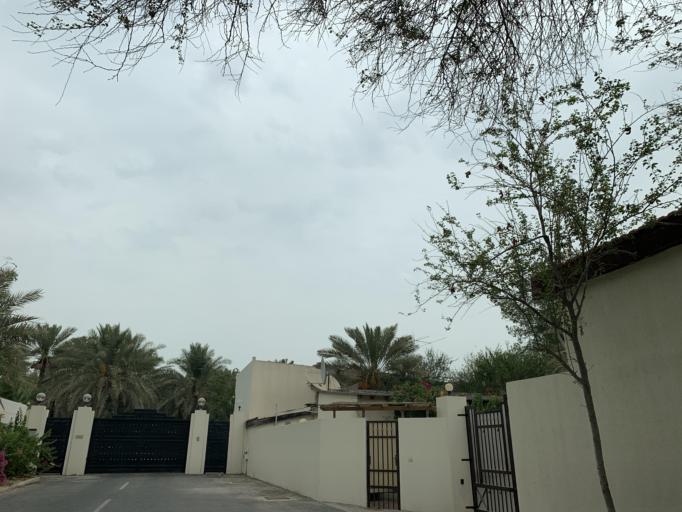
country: BH
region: Northern
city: Madinat `Isa
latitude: 26.1918
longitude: 50.4677
